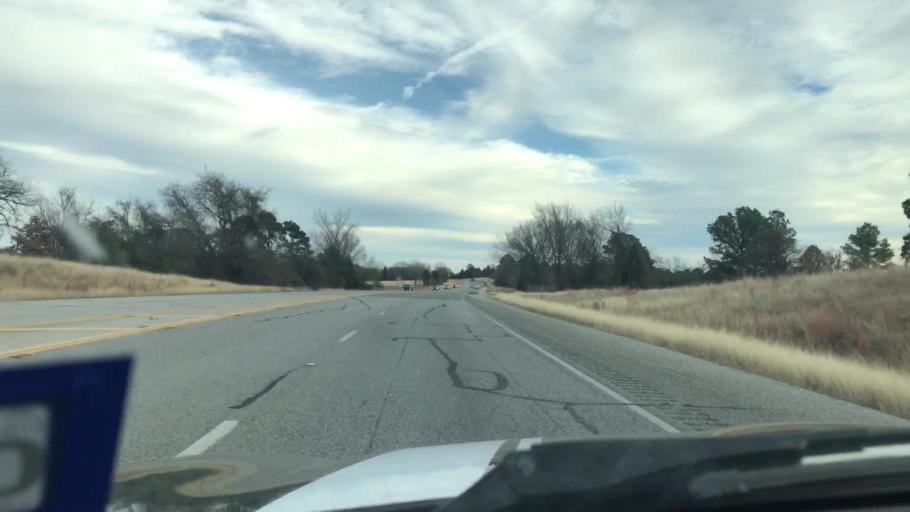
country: US
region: Texas
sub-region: Bastrop County
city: Elgin
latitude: 30.3021
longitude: -97.2928
